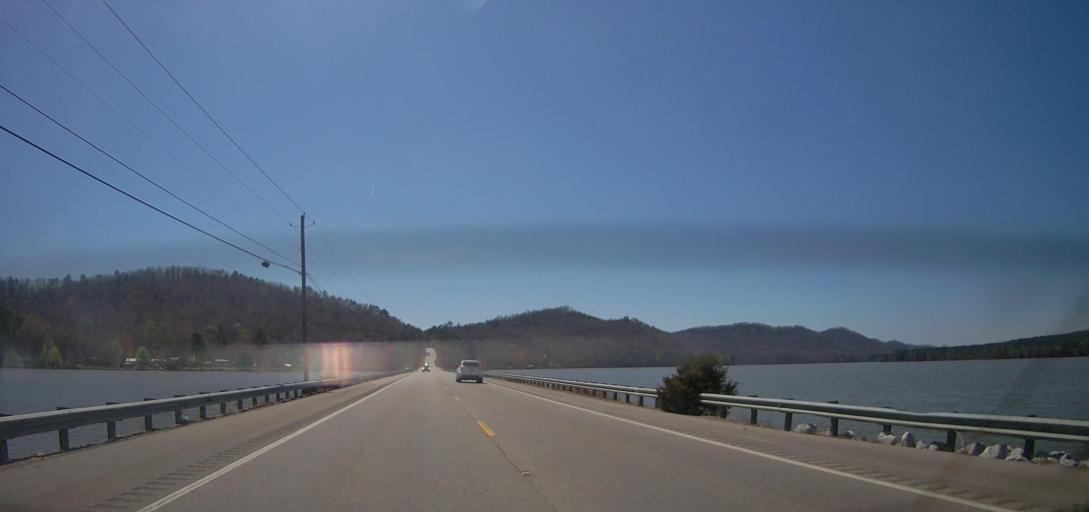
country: US
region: Alabama
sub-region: Etowah County
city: Southside
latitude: 33.8528
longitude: -86.0464
